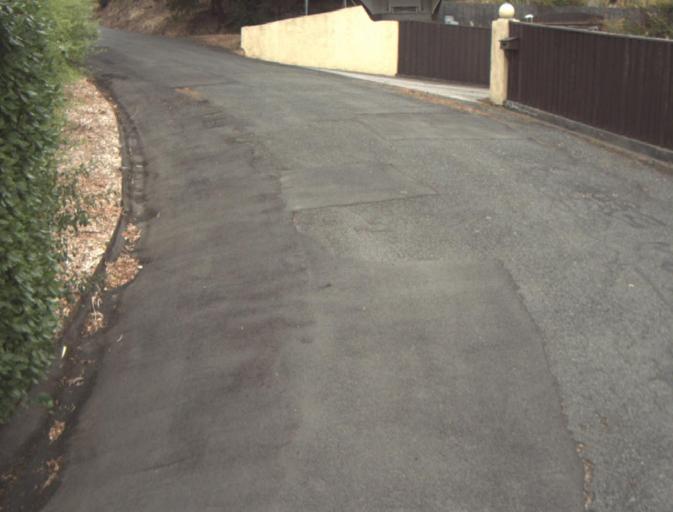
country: AU
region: Tasmania
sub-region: Launceston
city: Mayfield
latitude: -41.3301
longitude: 147.0672
